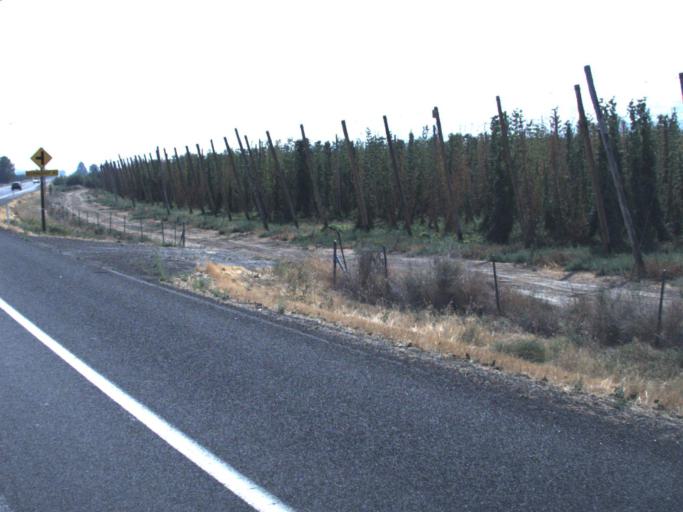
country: US
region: Washington
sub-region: Yakima County
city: Terrace Heights
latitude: 46.5494
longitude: -120.3373
